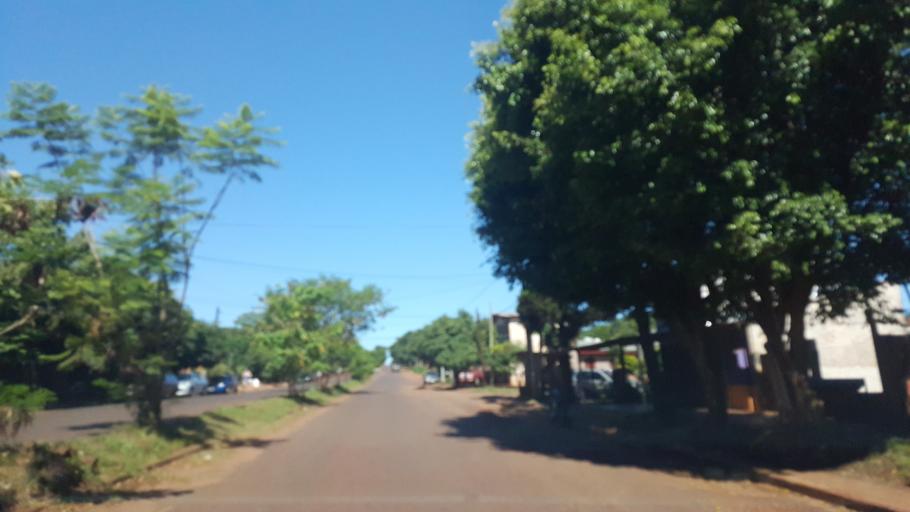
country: AR
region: Misiones
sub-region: Departamento de Capital
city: Posadas
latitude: -27.3883
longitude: -55.9248
